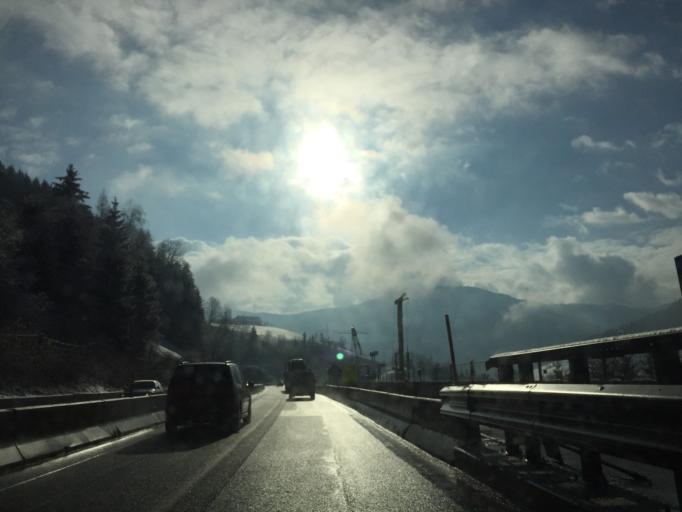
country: AT
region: Salzburg
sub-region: Politischer Bezirk Sankt Johann im Pongau
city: Huttau
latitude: 47.4245
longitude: 13.3004
